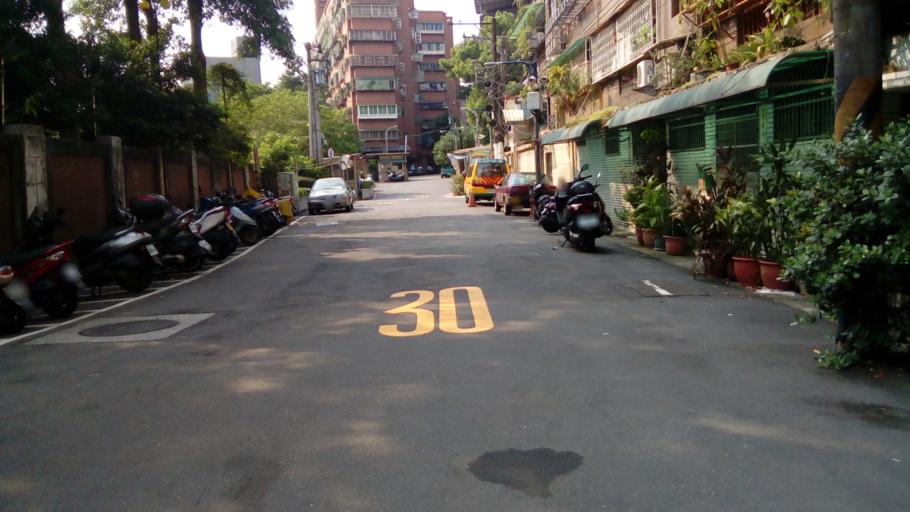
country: TW
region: Taipei
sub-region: Taipei
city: Banqiao
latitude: 25.0010
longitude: 121.4796
